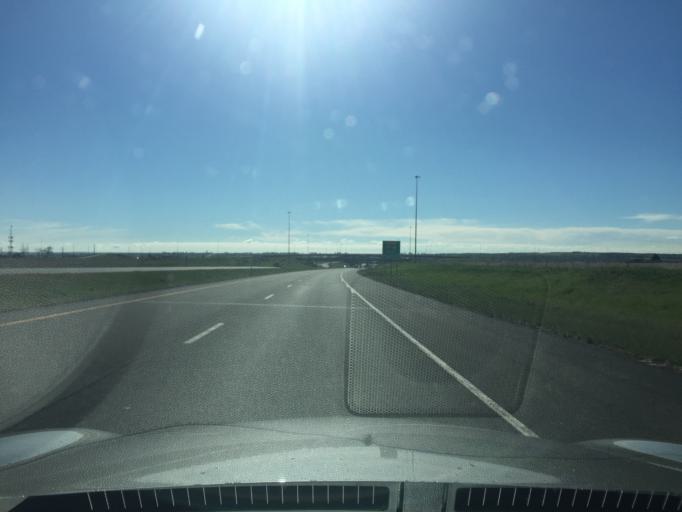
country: US
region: Colorado
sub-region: Boulder County
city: Erie
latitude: 39.9845
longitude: -105.0039
